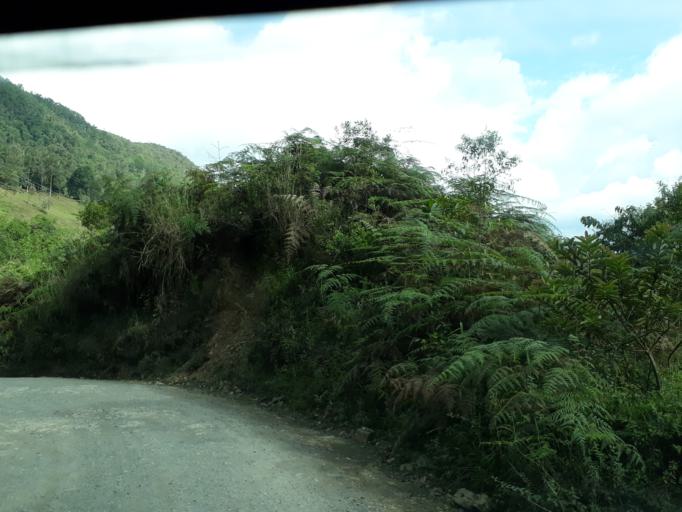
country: CO
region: Cundinamarca
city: Pacho
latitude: 5.2295
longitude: -74.1880
